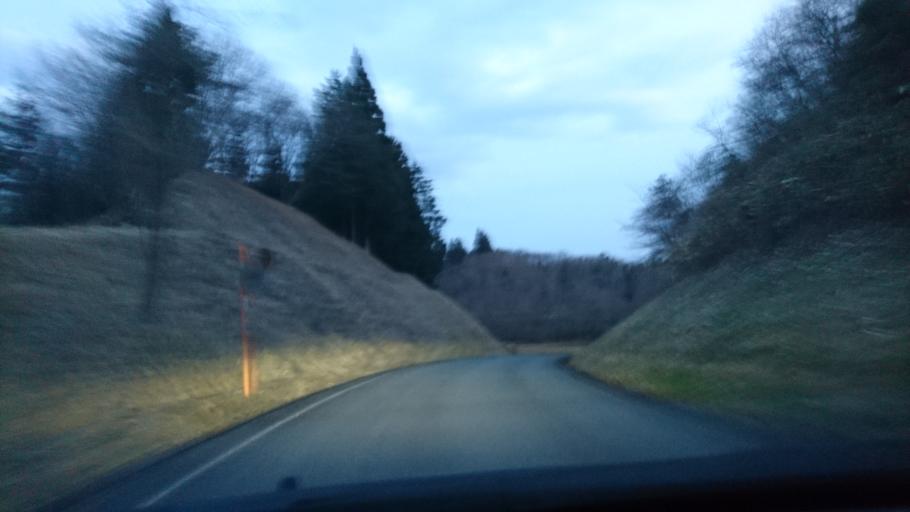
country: JP
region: Iwate
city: Ichinoseki
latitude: 38.9066
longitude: 141.3479
